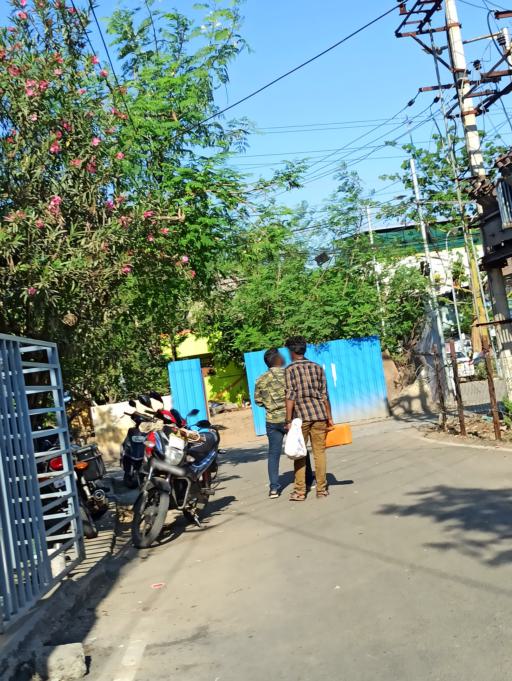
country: IN
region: Tamil Nadu
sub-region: Kancheepuram
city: Manappakkam
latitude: 13.0196
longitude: 80.1660
